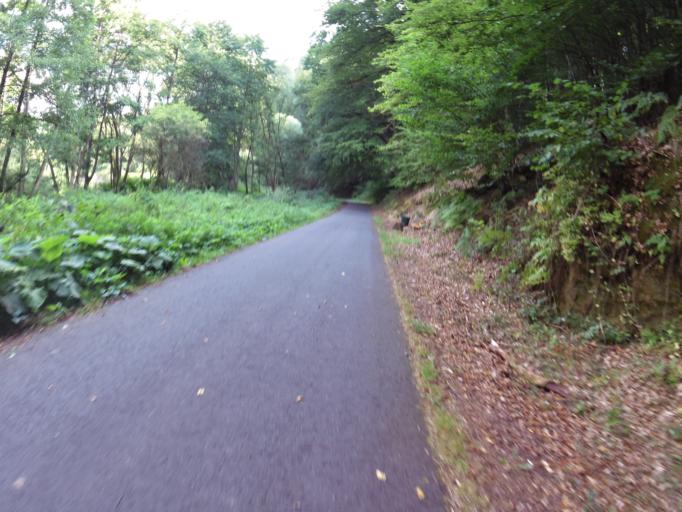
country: DE
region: Rheinland-Pfalz
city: Kordel
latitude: 49.8204
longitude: 6.6497
